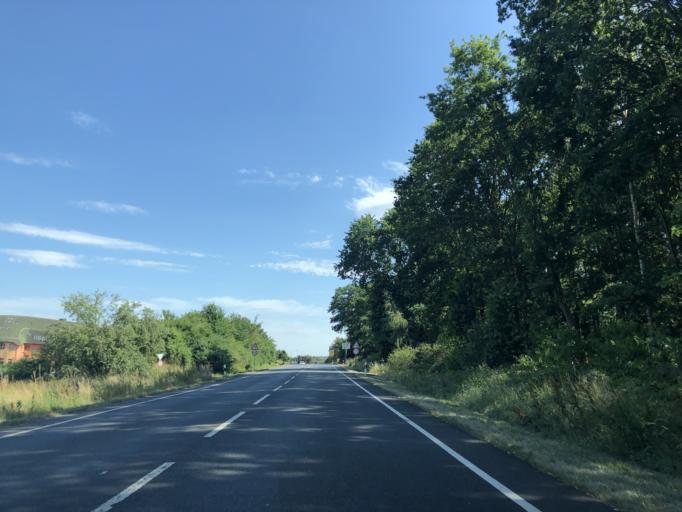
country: DE
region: Hesse
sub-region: Regierungsbezirk Darmstadt
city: Dietzenbach
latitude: 50.0242
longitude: 8.7697
